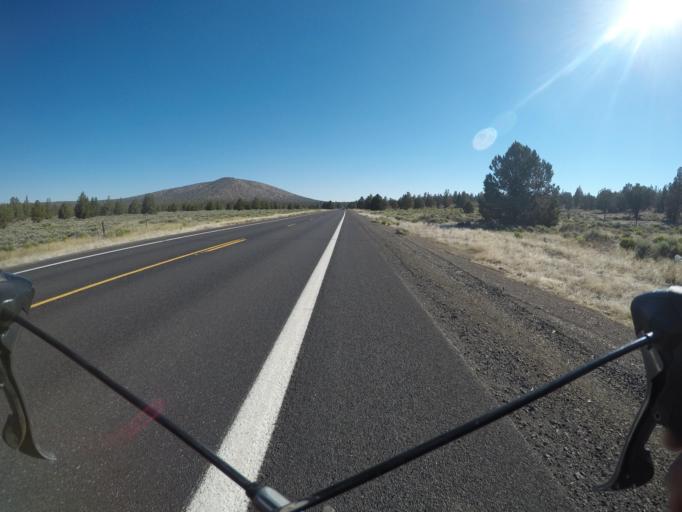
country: US
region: Oregon
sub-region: Deschutes County
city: Redmond
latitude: 44.2280
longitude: -121.3070
